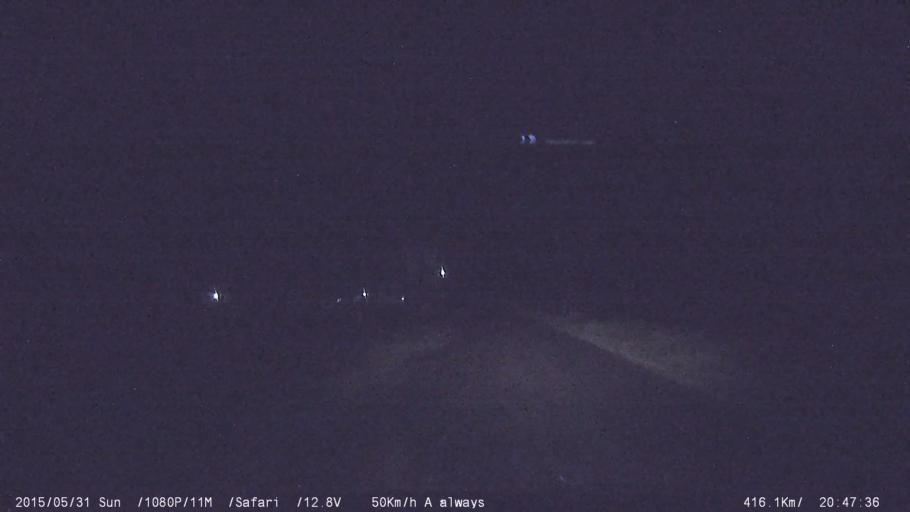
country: IN
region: Karnataka
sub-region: Ramanagara
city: Channapatna
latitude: 12.5643
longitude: 77.2214
